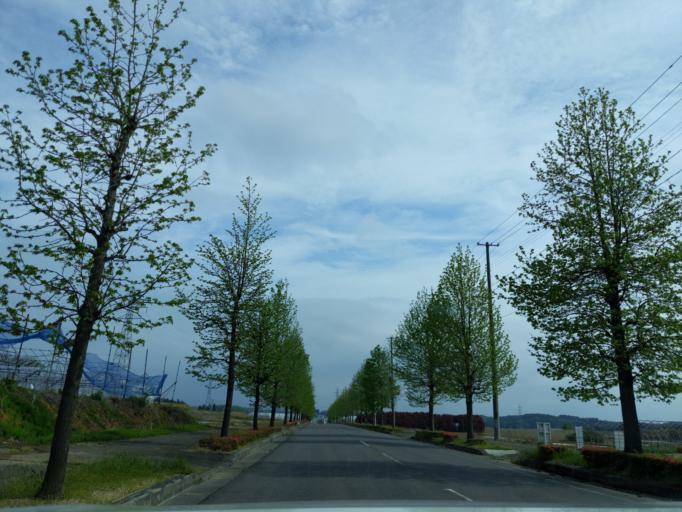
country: JP
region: Fukushima
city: Sukagawa
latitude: 37.3375
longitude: 140.3385
